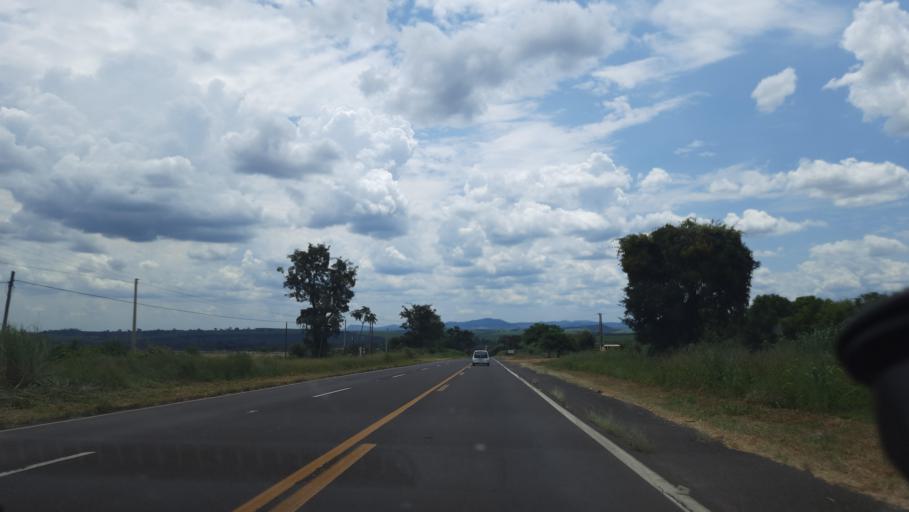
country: BR
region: Sao Paulo
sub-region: Mococa
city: Mococa
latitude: -21.4830
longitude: -47.0833
